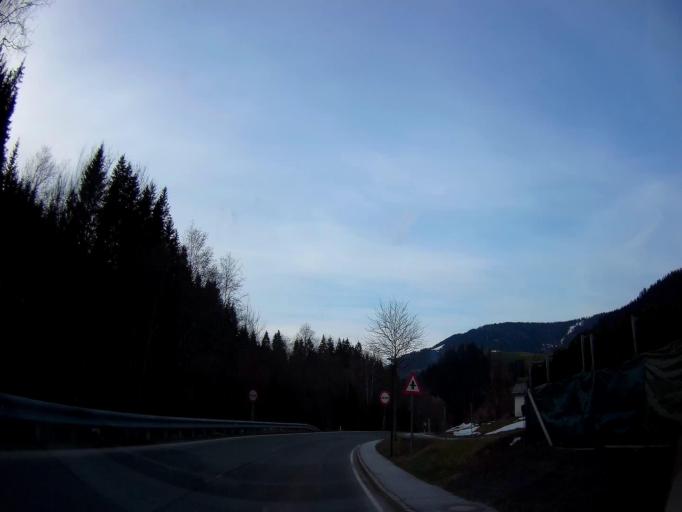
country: AT
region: Salzburg
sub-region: Politischer Bezirk Hallein
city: Abtenau
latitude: 47.5296
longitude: 13.4252
